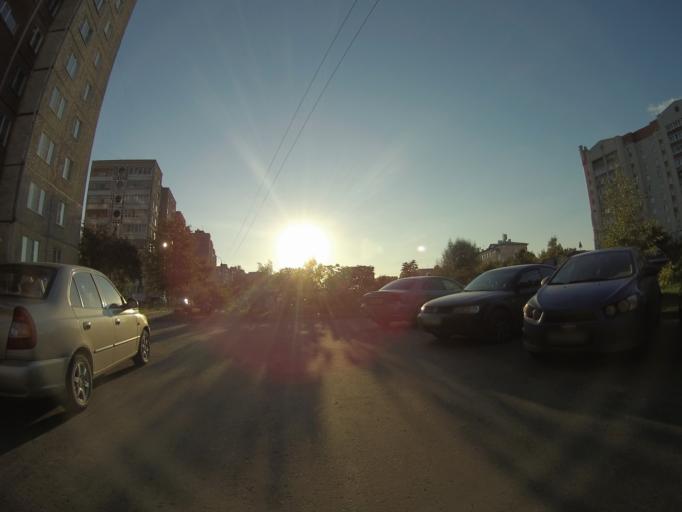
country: RU
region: Vladimir
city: Vladimir
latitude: 56.1097
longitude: 40.3518
